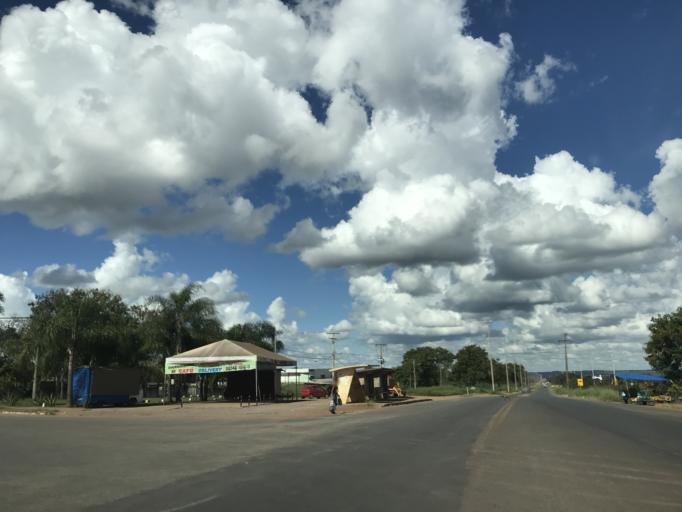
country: BR
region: Federal District
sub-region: Brasilia
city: Brasilia
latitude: -15.7531
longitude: -47.7542
